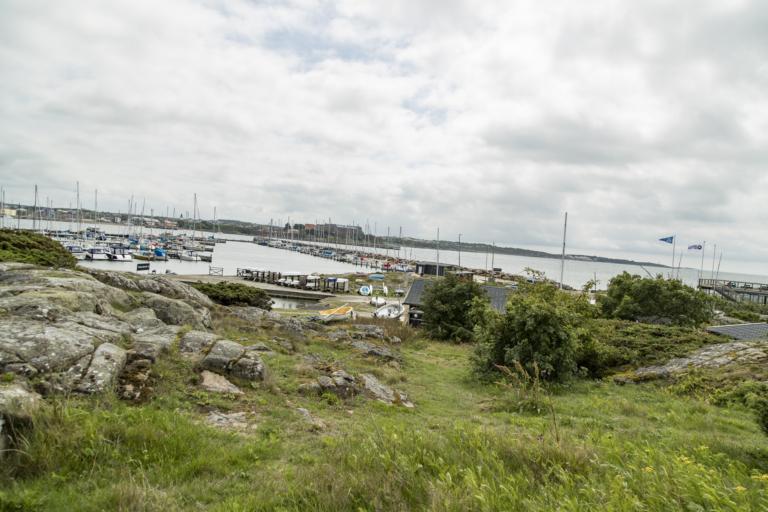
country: SE
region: Halland
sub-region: Varbergs Kommun
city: Varberg
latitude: 57.1124
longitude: 12.2263
